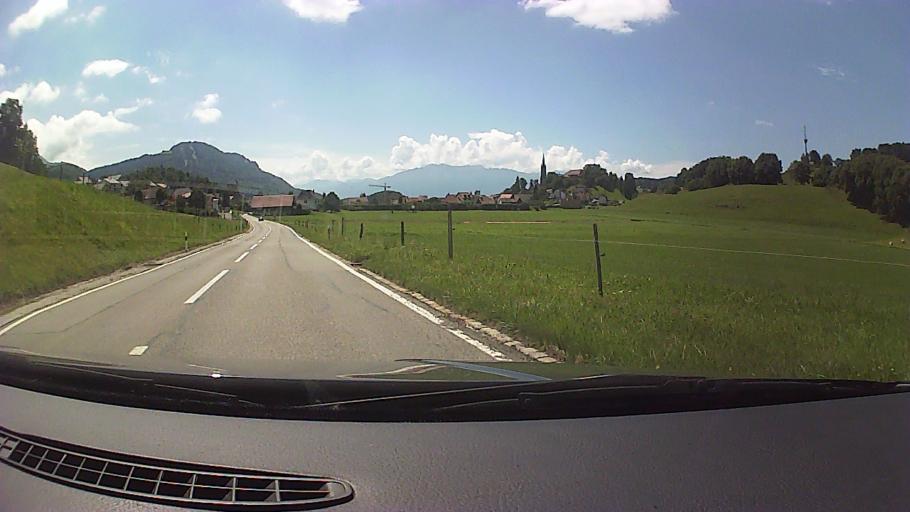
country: CH
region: Fribourg
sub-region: Veveyse District
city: Chatel-Saint-Denis
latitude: 46.5351
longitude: 6.9067
